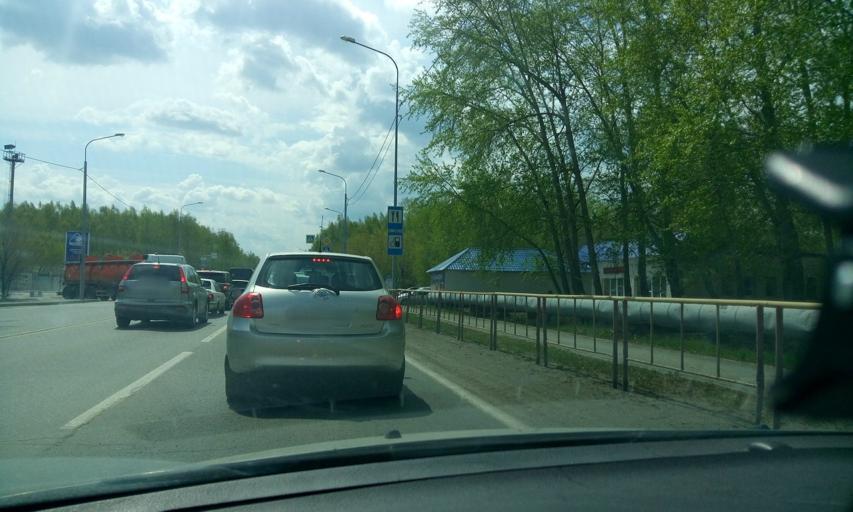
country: RU
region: Tjumen
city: Melioratorov
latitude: 57.1843
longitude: 65.5924
